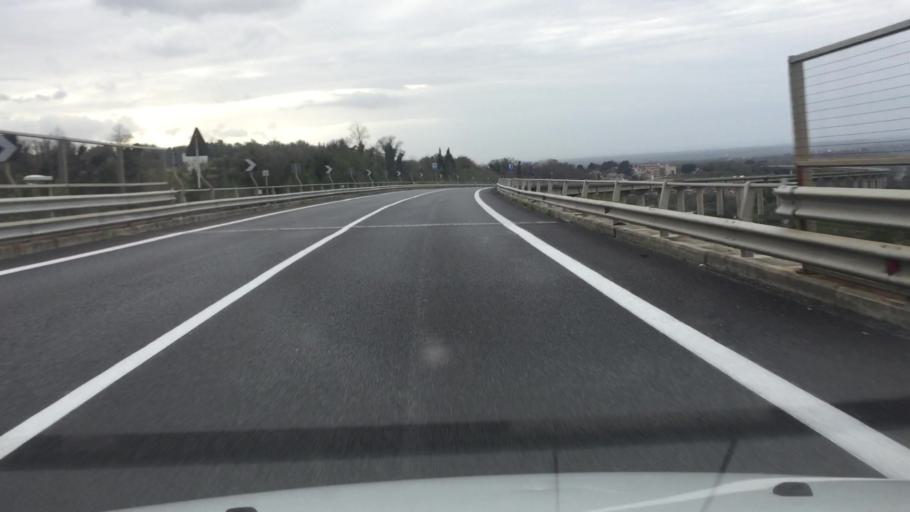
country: IT
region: Calabria
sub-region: Provincia di Reggio Calabria
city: Anoia Superiore
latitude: 38.4166
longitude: 16.1096
